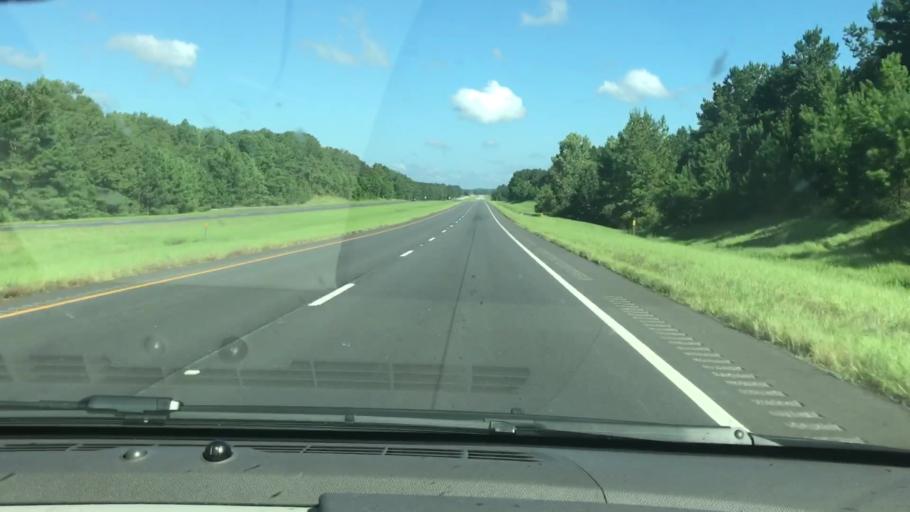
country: US
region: Alabama
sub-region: Barbour County
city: Eufaula
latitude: 32.0534
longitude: -85.1350
